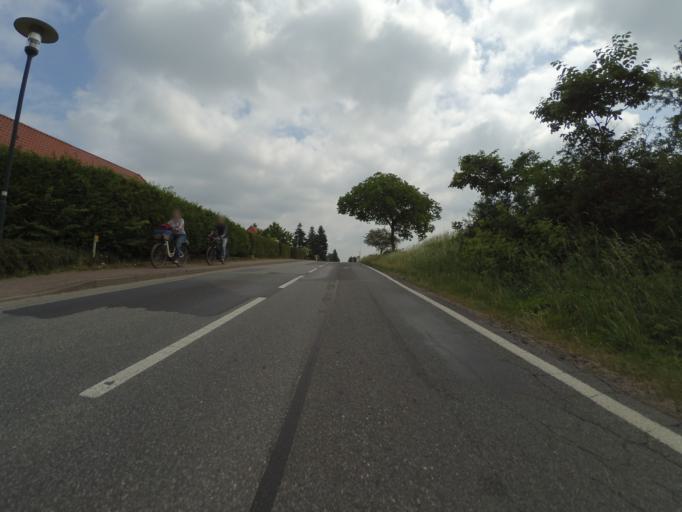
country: DE
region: Mecklenburg-Vorpommern
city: Malchow
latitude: 53.5212
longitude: 12.4497
